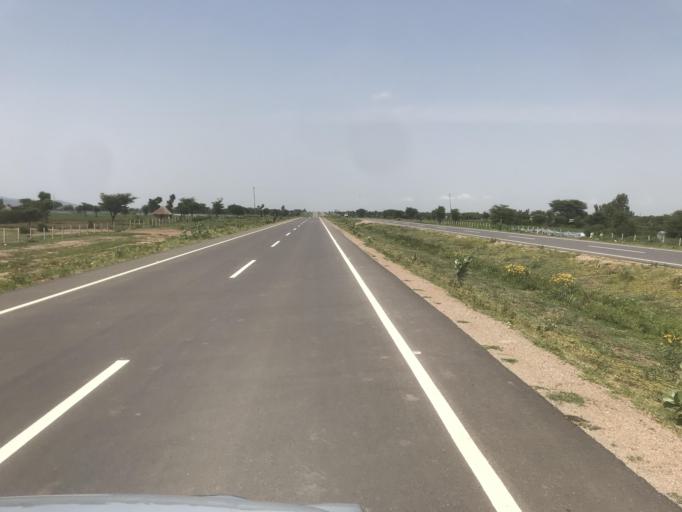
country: ET
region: Oromiya
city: Mojo
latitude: 8.3771
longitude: 39.0011
